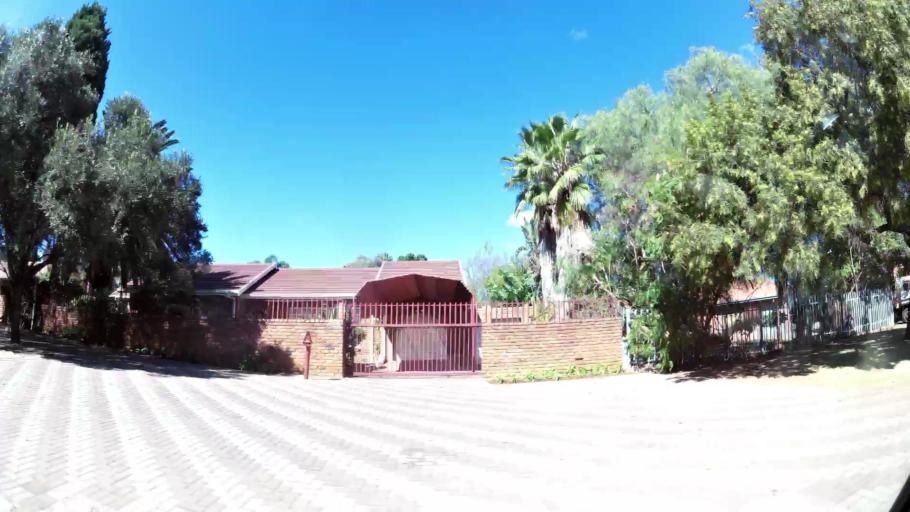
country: ZA
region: Limpopo
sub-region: Capricorn District Municipality
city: Polokwane
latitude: -23.9118
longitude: 29.4838
